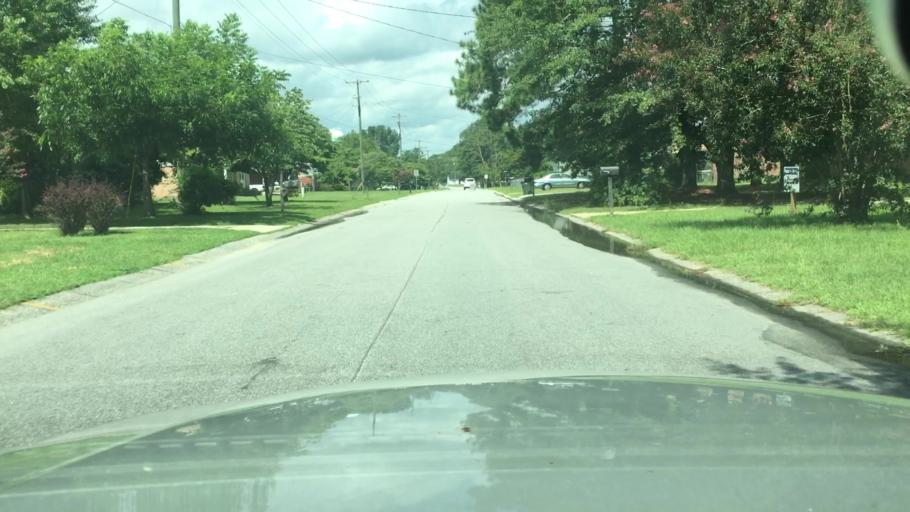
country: US
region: North Carolina
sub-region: Cumberland County
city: Hope Mills
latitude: 35.0324
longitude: -78.9924
